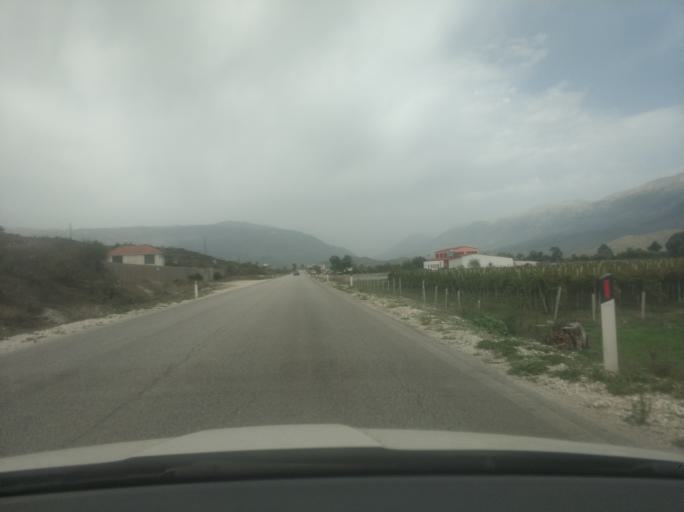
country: AL
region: Gjirokaster
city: Gjirokaster
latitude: 40.1104
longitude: 20.1216
